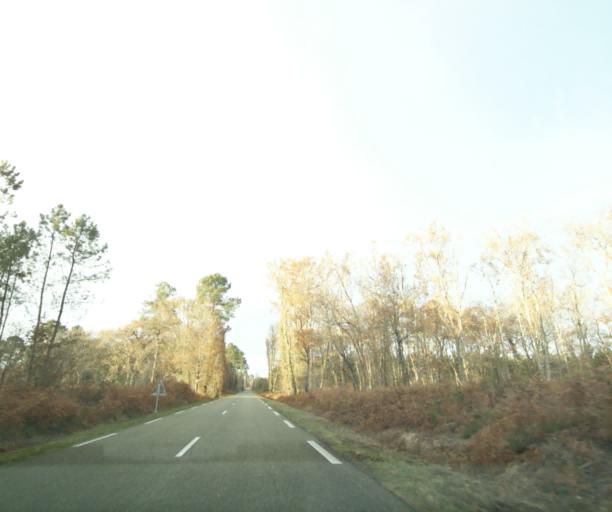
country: FR
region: Aquitaine
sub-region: Departement des Landes
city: Gabarret
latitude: 44.0553
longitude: -0.0454
